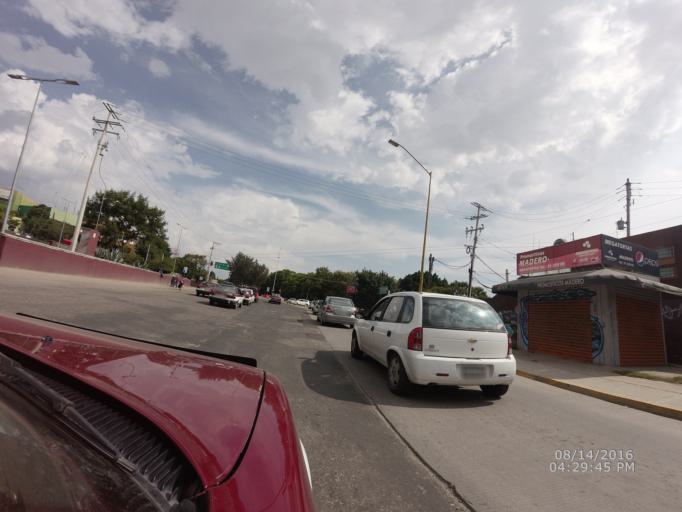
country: MX
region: Oaxaca
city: Oaxaca de Juarez
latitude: 17.0806
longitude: -96.7435
